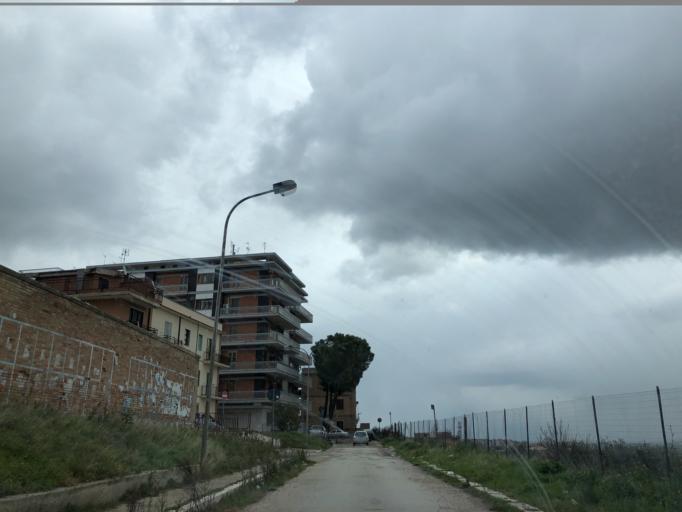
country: IT
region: Apulia
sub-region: Provincia di Foggia
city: Lucera
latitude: 41.5061
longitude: 15.3283
